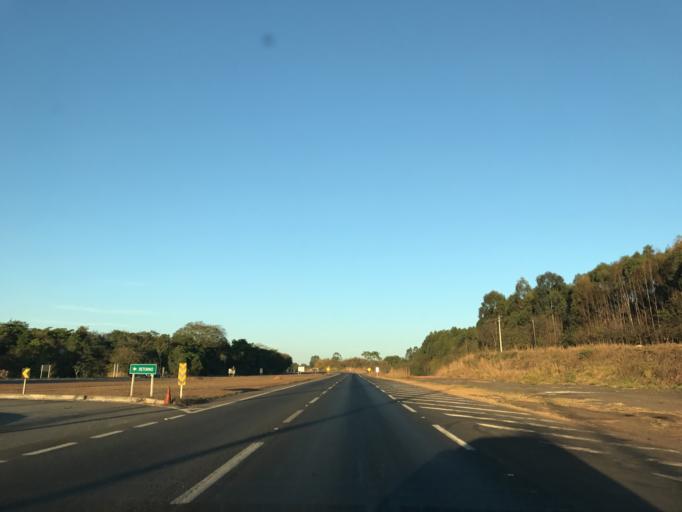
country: BR
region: Goias
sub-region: Anapolis
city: Anapolis
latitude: -16.3203
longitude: -48.8713
